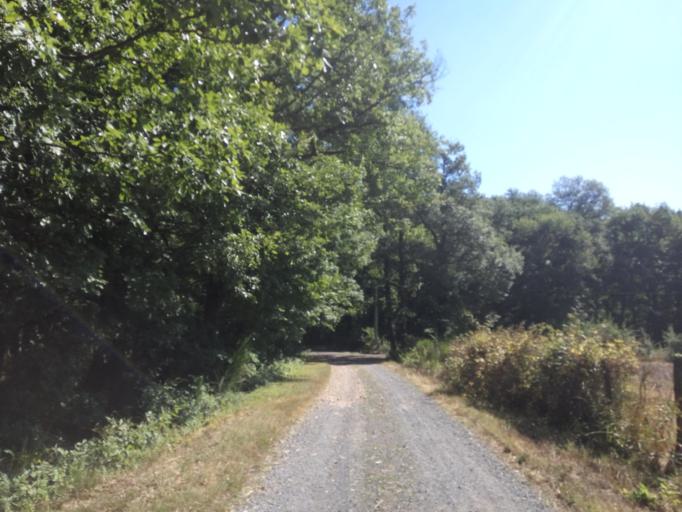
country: FR
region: Auvergne
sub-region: Departement de l'Allier
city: Brugheas
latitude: 46.0894
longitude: 3.3590
